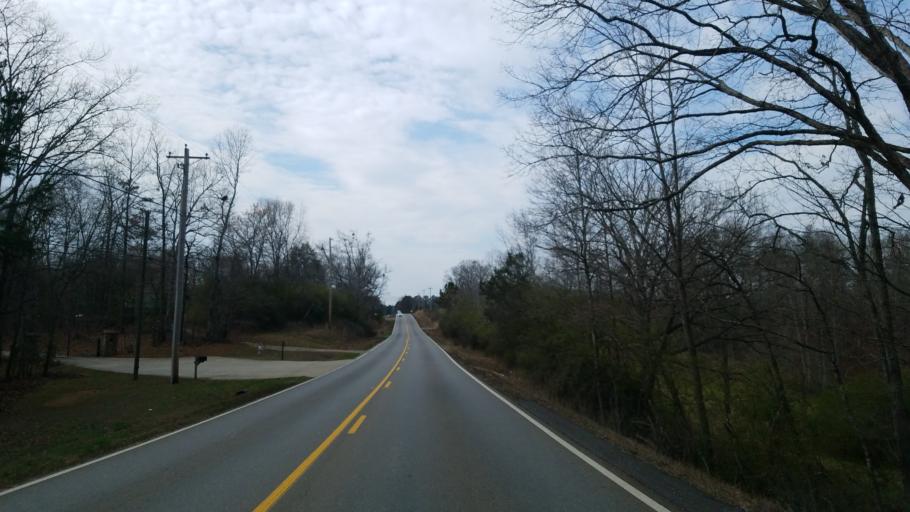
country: US
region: Georgia
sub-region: Cherokee County
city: Ball Ground
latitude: 34.2990
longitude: -84.3192
